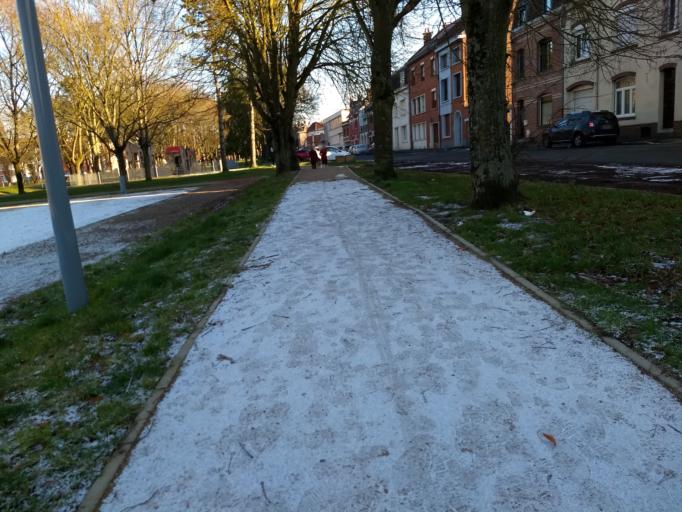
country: FR
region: Nord-Pas-de-Calais
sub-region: Departement du Pas-de-Calais
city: Arras
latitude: 50.2864
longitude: 2.7860
